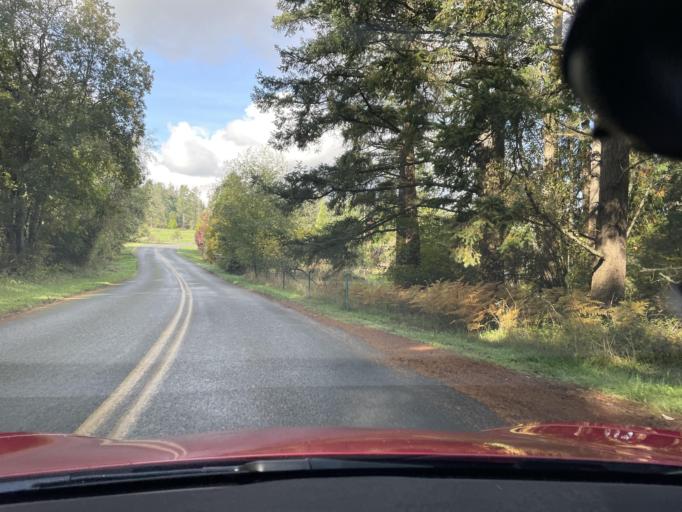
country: US
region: Washington
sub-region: San Juan County
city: Friday Harbor
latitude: 48.5055
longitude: -123.0189
